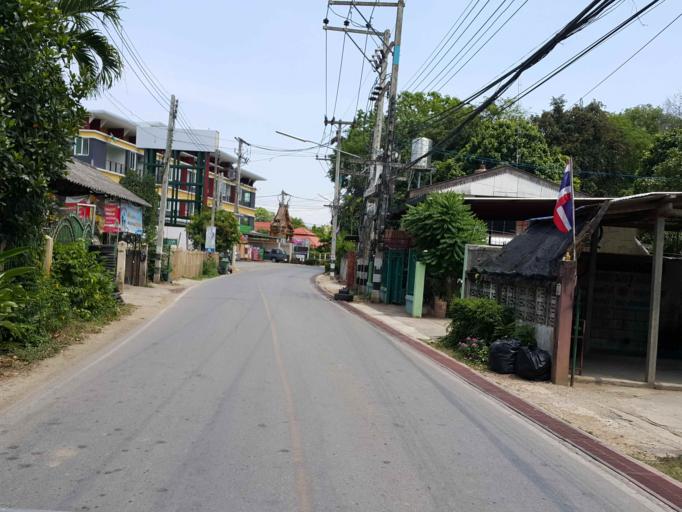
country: TH
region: Chiang Mai
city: Chiang Mai
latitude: 18.8426
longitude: 98.9887
